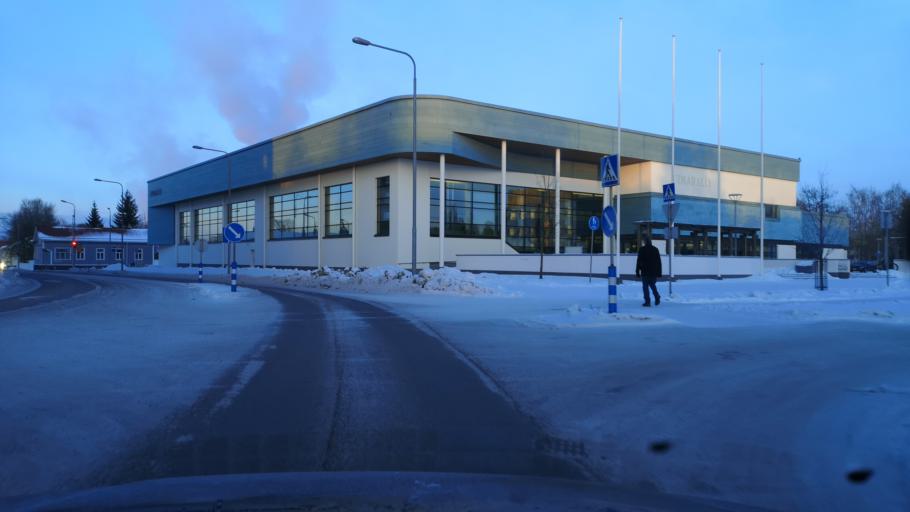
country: FI
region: Satakunta
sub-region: Pori
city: Pori
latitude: 61.4796
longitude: 21.8050
